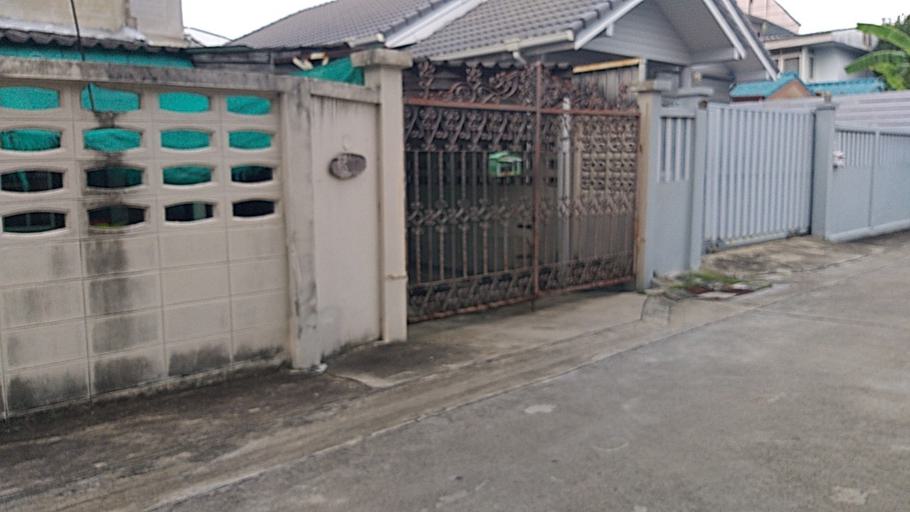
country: TH
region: Bangkok
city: Suan Luang
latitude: 13.7108
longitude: 100.6608
